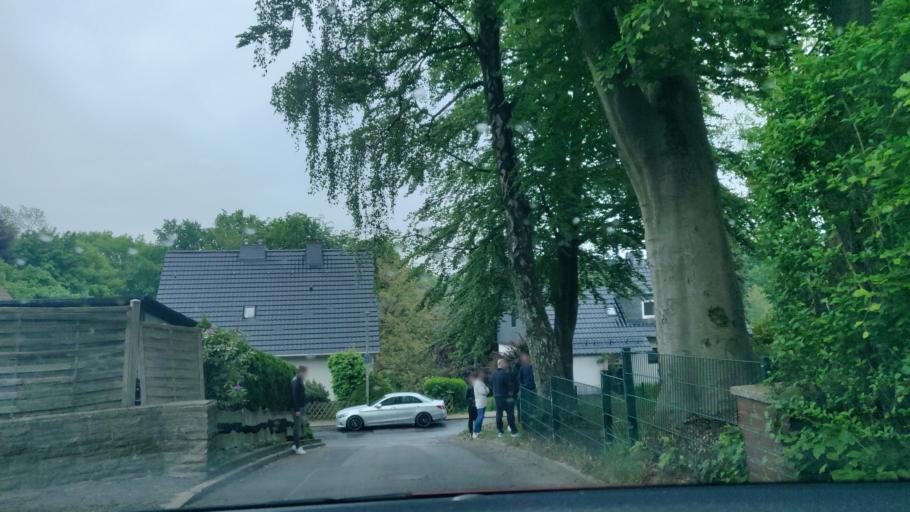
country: DE
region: North Rhine-Westphalia
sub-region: Regierungsbezirk Dusseldorf
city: Heiligenhaus
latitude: 51.3330
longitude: 6.9590
